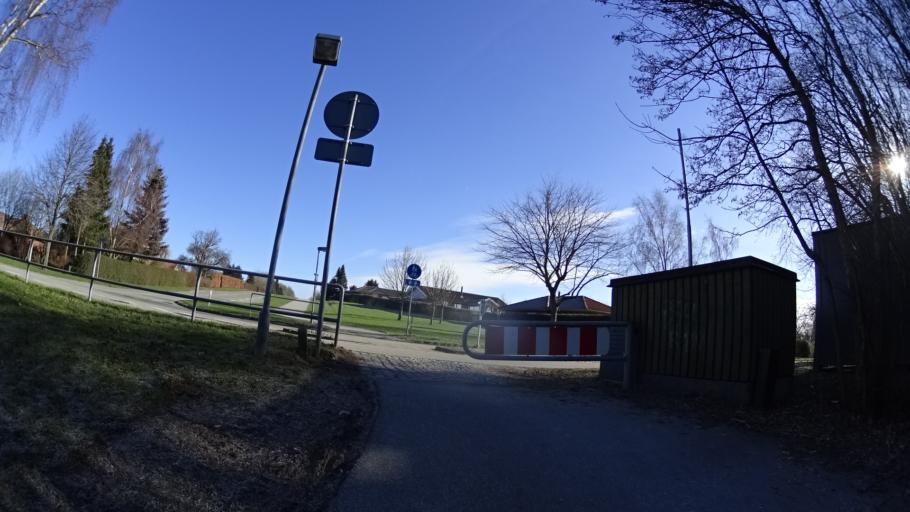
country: DK
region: Central Jutland
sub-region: Arhus Kommune
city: Kolt
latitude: 56.1075
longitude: 10.0846
